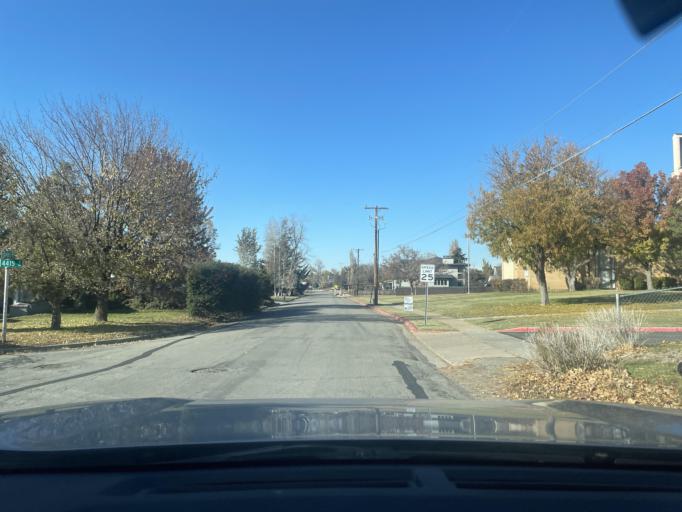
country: US
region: Utah
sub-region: Salt Lake County
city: Holladay
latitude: 40.6754
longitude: -111.8304
